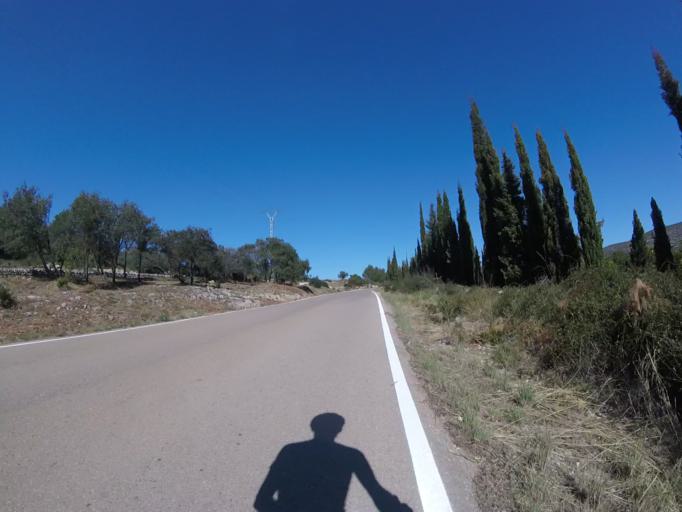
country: ES
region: Valencia
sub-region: Provincia de Castello
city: Santa Magdalena de Pulpis
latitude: 40.3666
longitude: 0.2761
